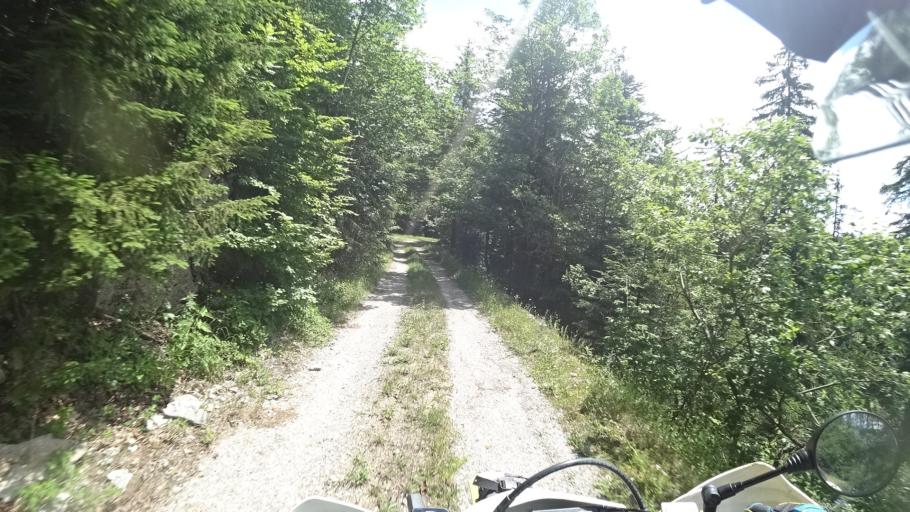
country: SI
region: Osilnica
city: Osilnica
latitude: 45.4764
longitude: 14.7151
